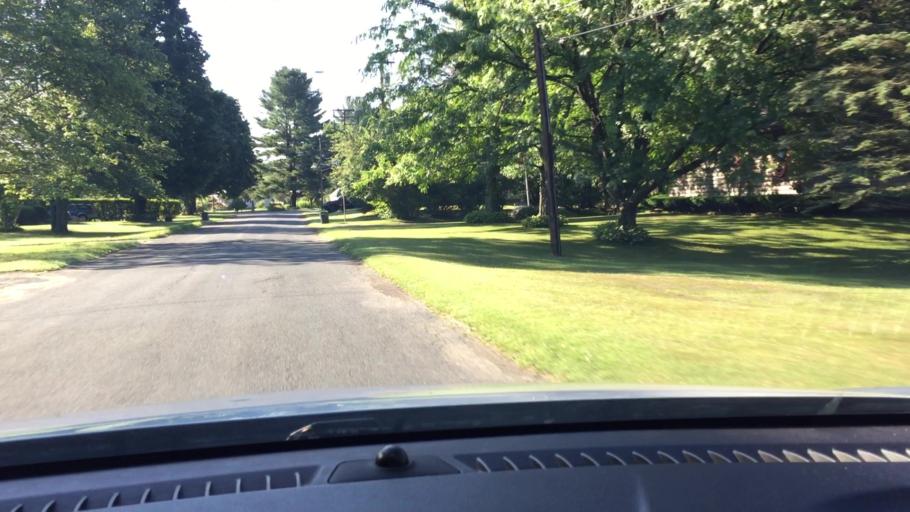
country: US
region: Massachusetts
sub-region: Berkshire County
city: Pittsfield
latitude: 42.4494
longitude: -73.2185
